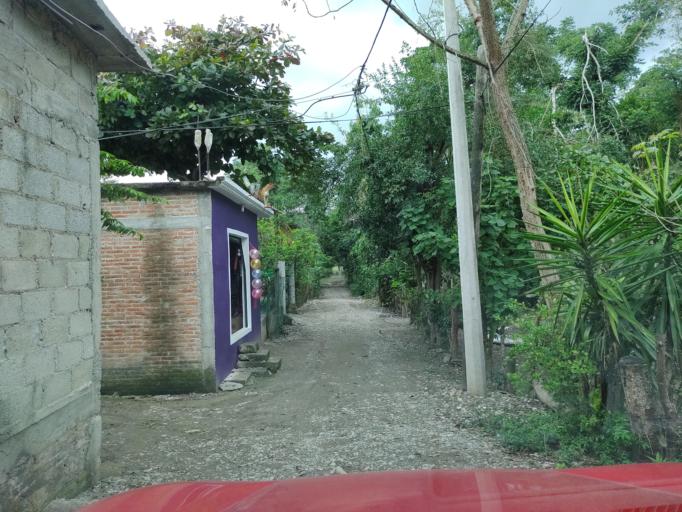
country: MX
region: Veracruz
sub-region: Papantla
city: El Chote
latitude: 20.4299
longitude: -97.3820
